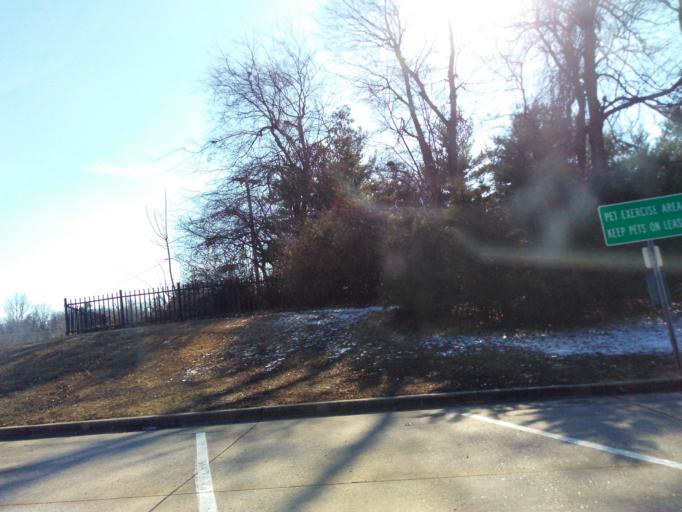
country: US
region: Kentucky
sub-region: McCracken County
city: Hendron
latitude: 37.0506
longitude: -88.6532
